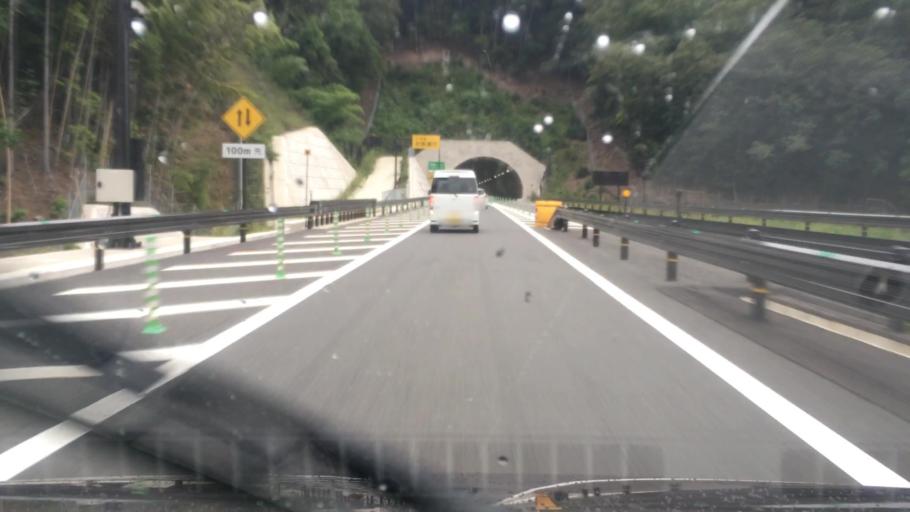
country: JP
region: Hyogo
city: Toyooka
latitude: 35.4340
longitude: 134.7677
